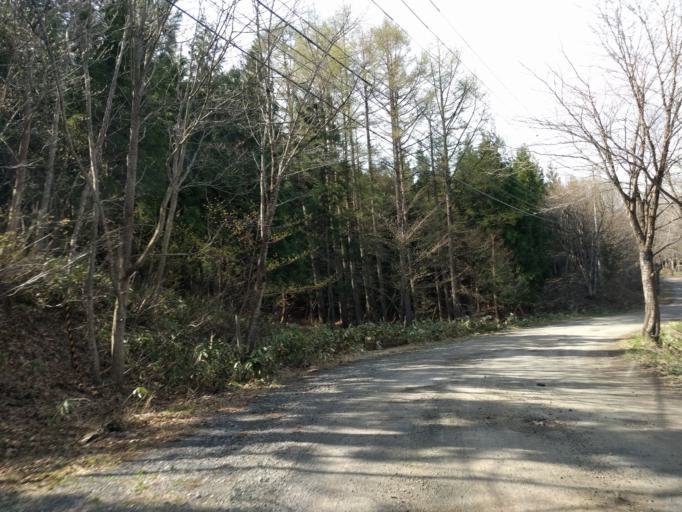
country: JP
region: Fukushima
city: Inawashiro
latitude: 37.5262
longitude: 140.0369
